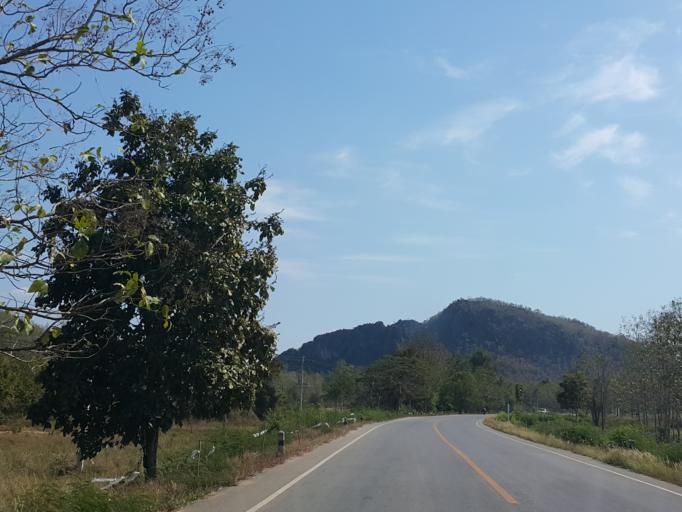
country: TH
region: Sukhothai
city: Thung Saliam
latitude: 17.3349
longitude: 99.4909
